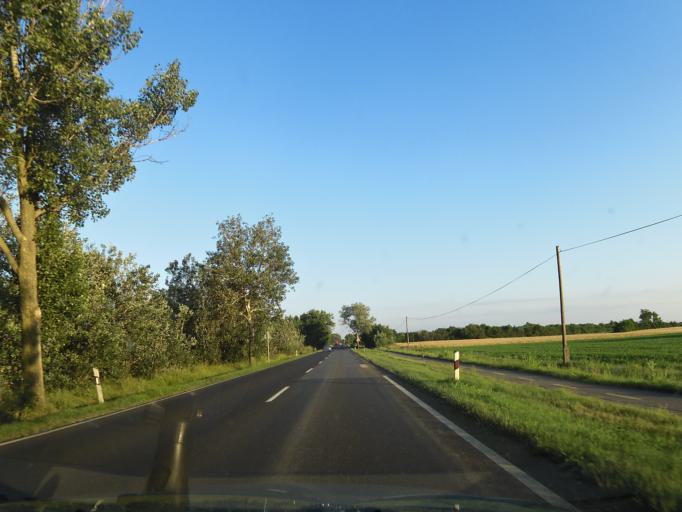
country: HU
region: Csongrad
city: Hodmezovasarhely
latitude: 46.4529
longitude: 20.3141
